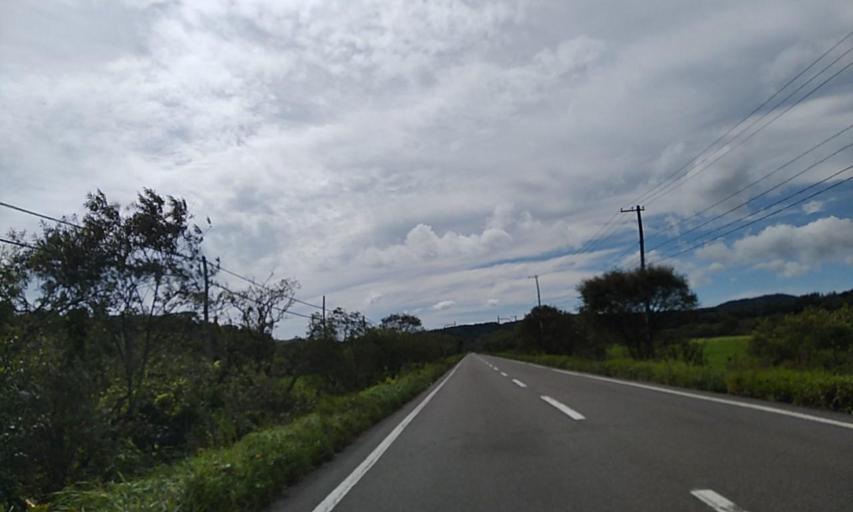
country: JP
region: Hokkaido
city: Kushiro
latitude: 42.8475
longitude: 143.8485
